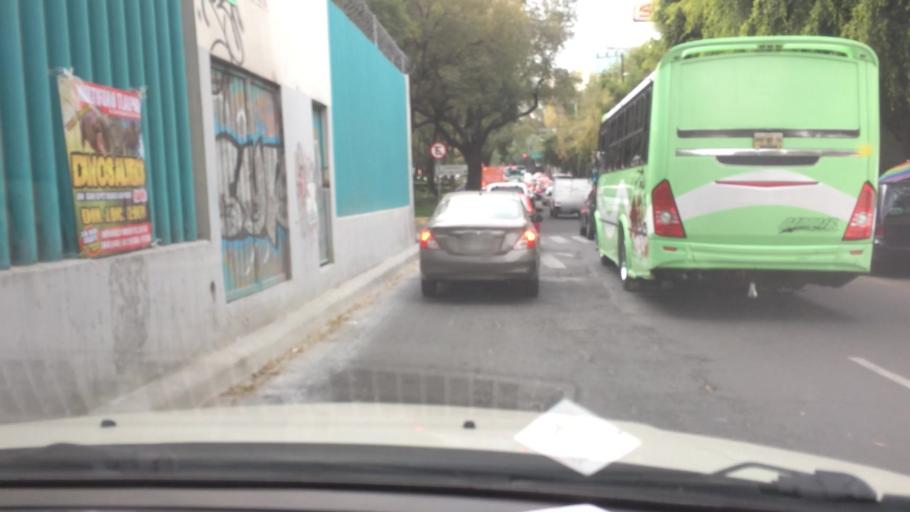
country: MX
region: Mexico City
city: Tlalpan
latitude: 19.2954
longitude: -99.1824
